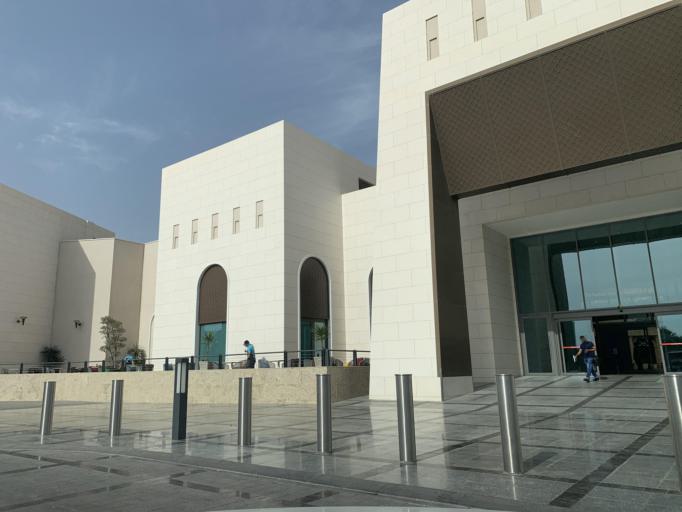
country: BH
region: Muharraq
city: Al Muharraq
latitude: 26.2476
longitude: 50.5865
